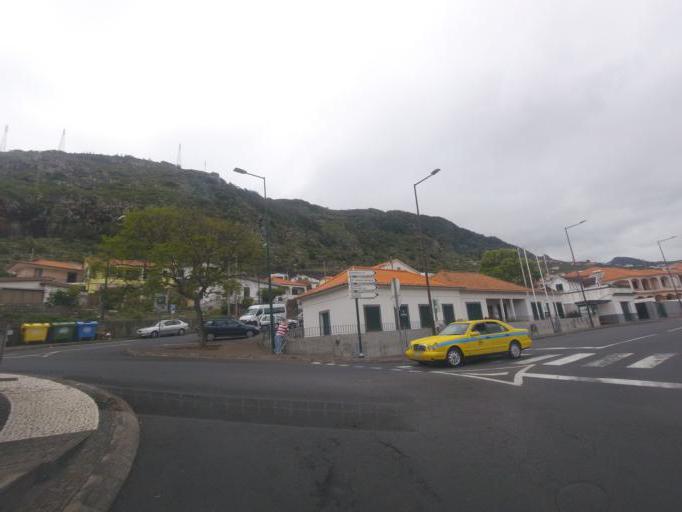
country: PT
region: Madeira
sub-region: Machico
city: Machico
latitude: 32.7174
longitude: -16.7670
